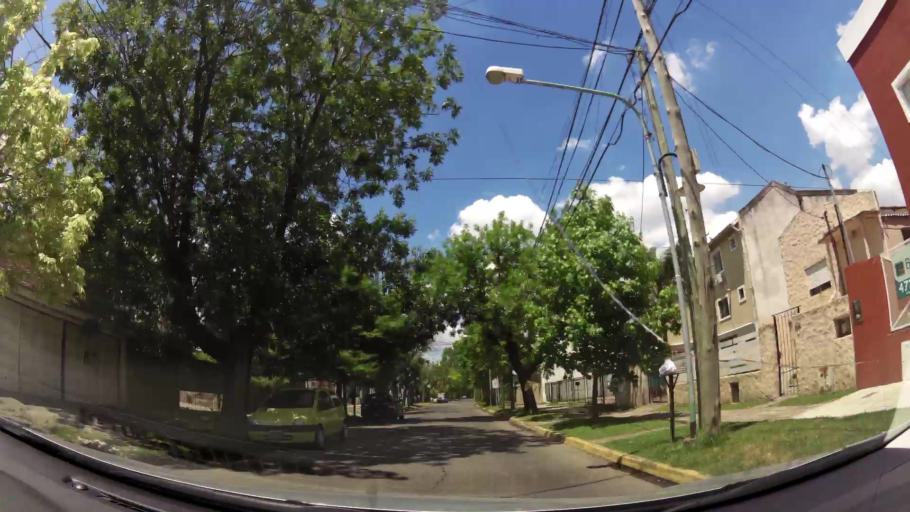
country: AR
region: Buenos Aires
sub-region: Partido de Tigre
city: Tigre
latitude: -34.4120
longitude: -58.5897
